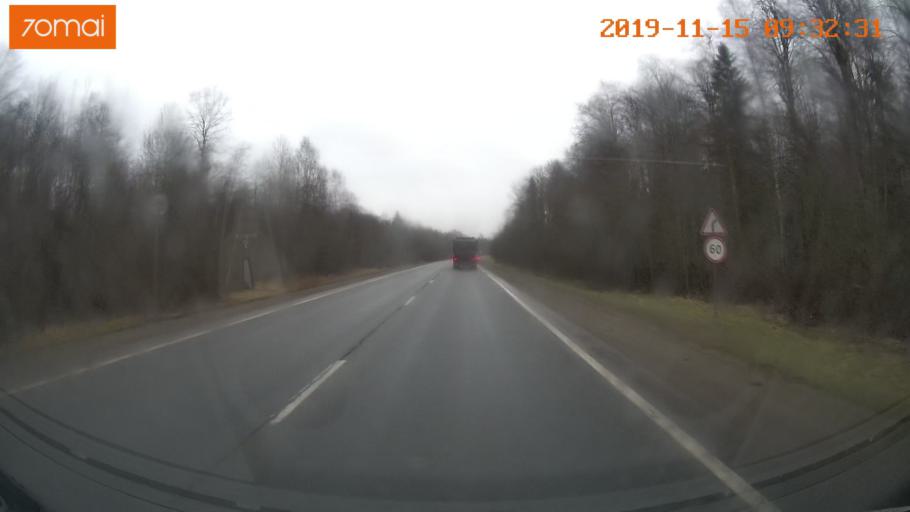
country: RU
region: Vologda
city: Sheksna
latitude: 59.2712
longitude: 38.3371
